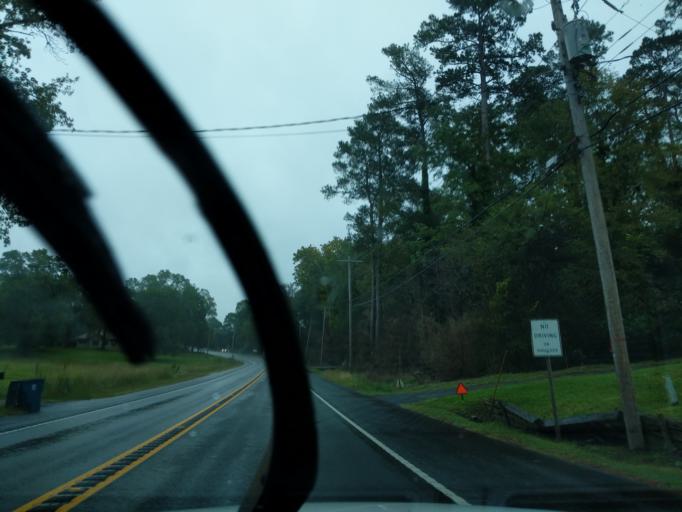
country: US
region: Louisiana
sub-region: Caddo Parish
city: Greenwood
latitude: 32.3737
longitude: -94.0374
